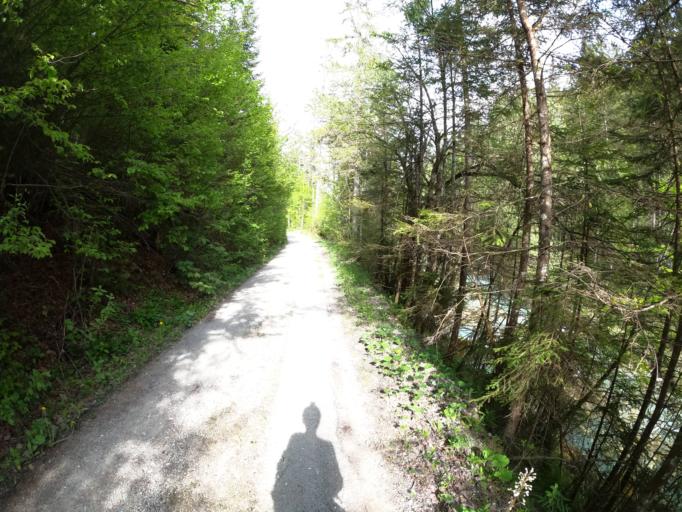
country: AT
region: Salzburg
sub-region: Politischer Bezirk Sankt Johann im Pongau
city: Werfen
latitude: 47.4772
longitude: 13.1166
